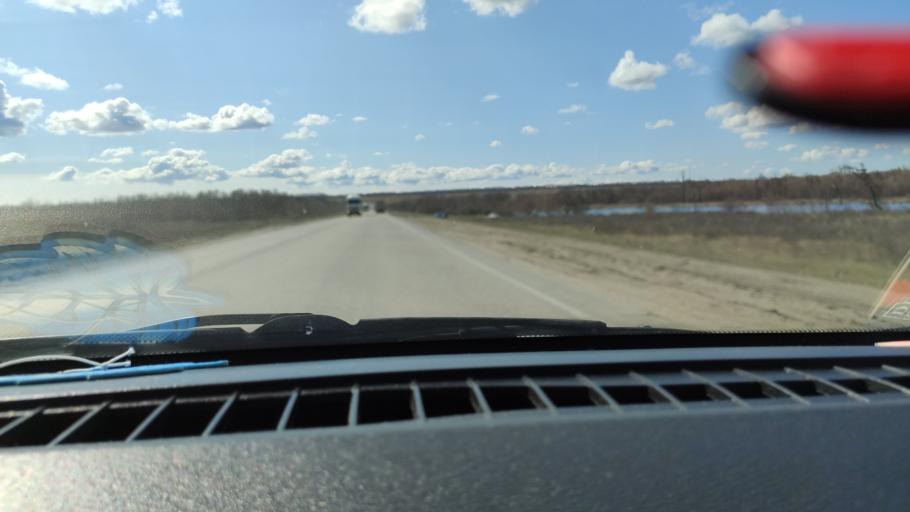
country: RU
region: Samara
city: Varlamovo
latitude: 53.1368
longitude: 48.2864
